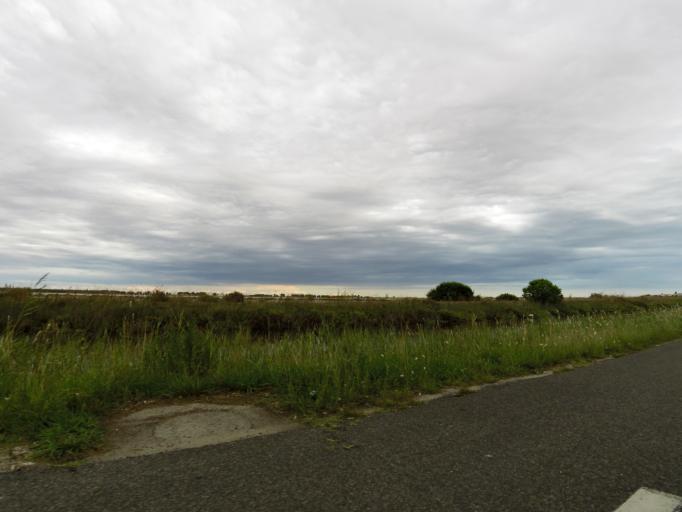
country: FR
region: Languedoc-Roussillon
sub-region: Departement du Gard
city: Le Grau-du-Roi
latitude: 43.5351
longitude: 4.1463
